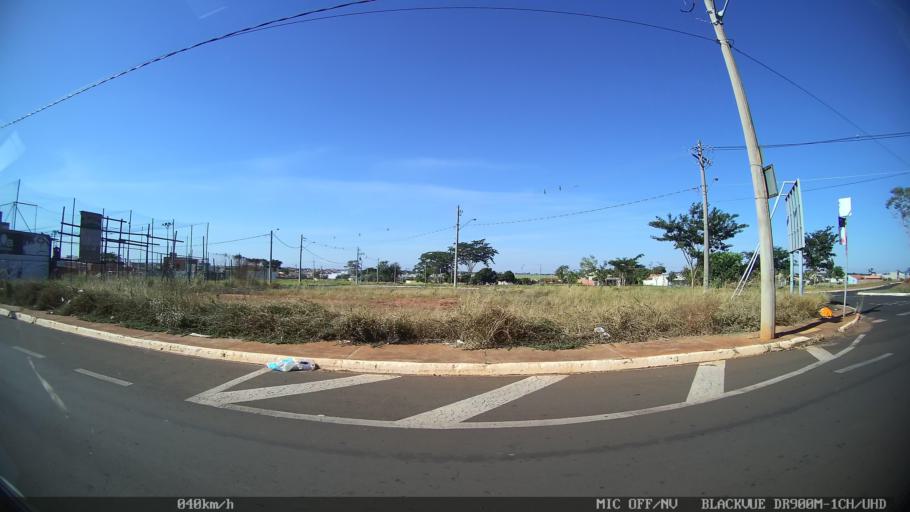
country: BR
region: Sao Paulo
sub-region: Olimpia
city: Olimpia
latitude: -20.7543
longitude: -48.9119
